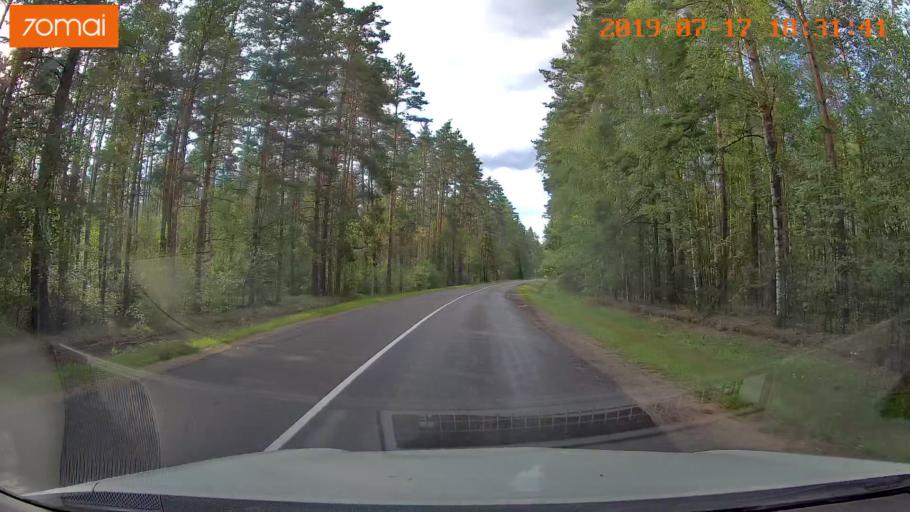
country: BY
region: Mogilev
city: Asipovichy
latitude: 53.2620
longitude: 28.6796
